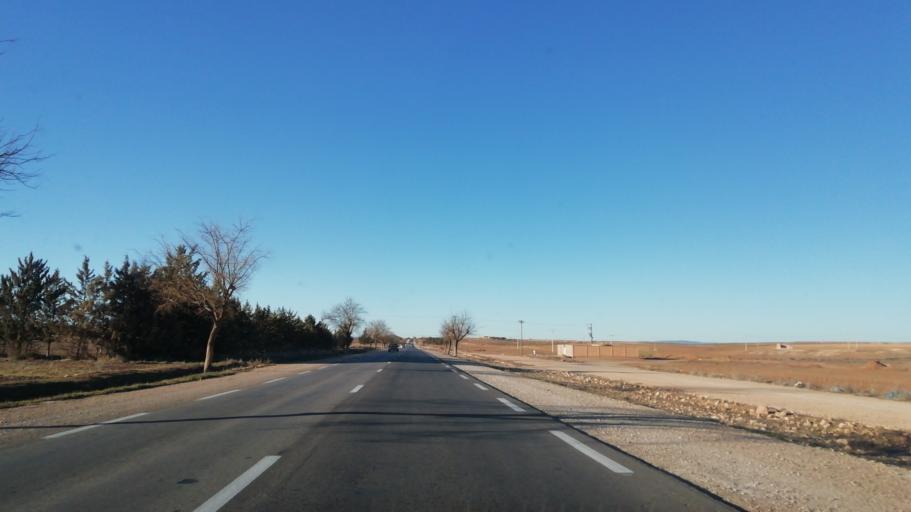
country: DZ
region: Tlemcen
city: Sebdou
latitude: 34.5178
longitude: -1.2873
